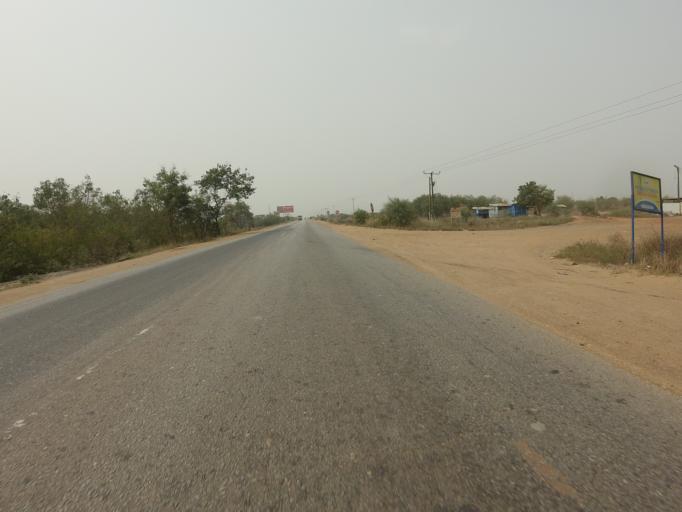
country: GH
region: Greater Accra
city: Tema
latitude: 5.8263
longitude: 0.1979
